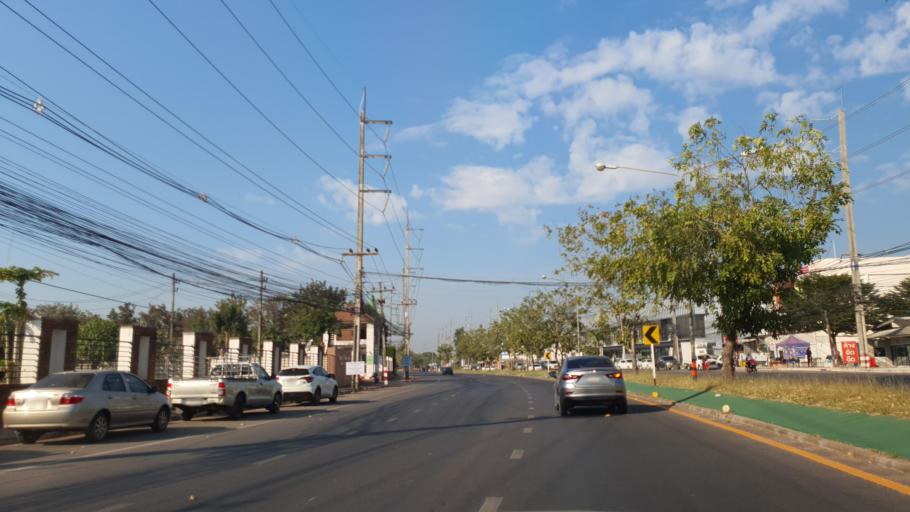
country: TH
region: Khon Kaen
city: Khon Kaen
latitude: 16.4116
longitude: 102.8104
